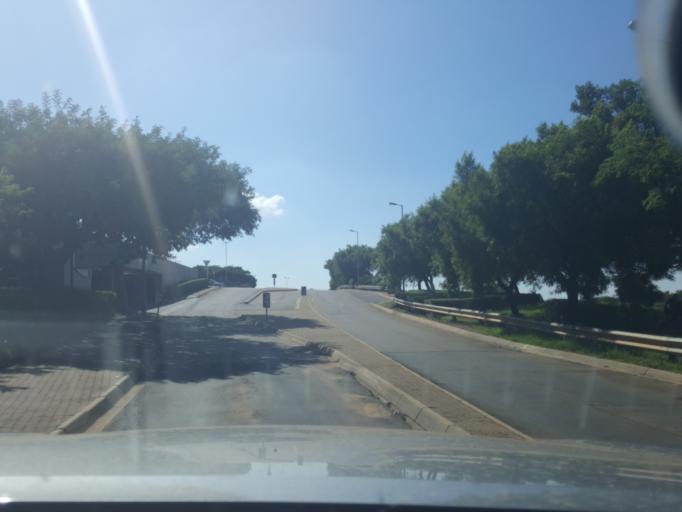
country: ZA
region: Gauteng
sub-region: City of Tshwane Metropolitan Municipality
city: Centurion
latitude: -25.8230
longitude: 28.3151
